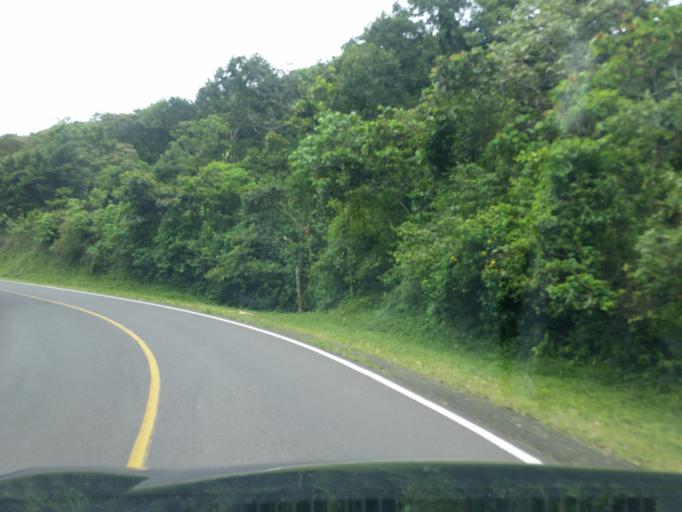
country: NI
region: Matagalpa
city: San Ramon
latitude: 12.9626
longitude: -85.8551
